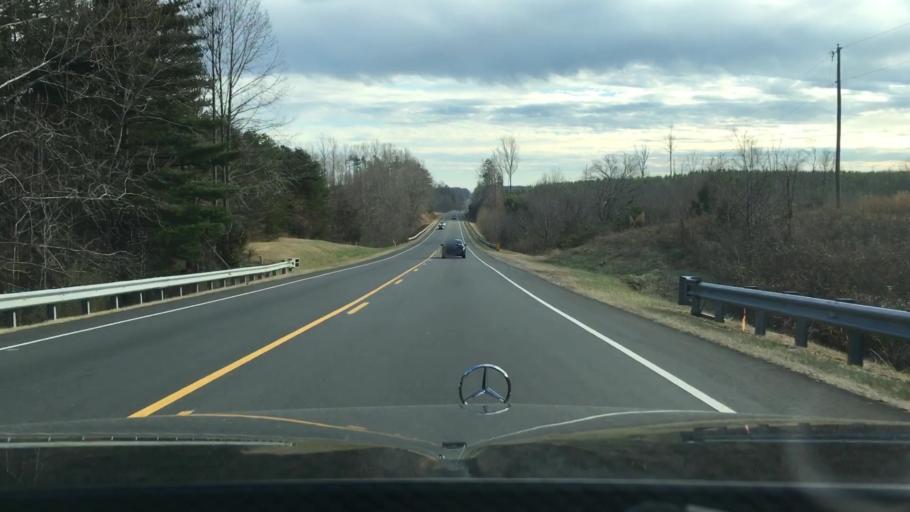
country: US
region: Virginia
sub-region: City of Danville
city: Danville
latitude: 36.5193
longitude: -79.3944
